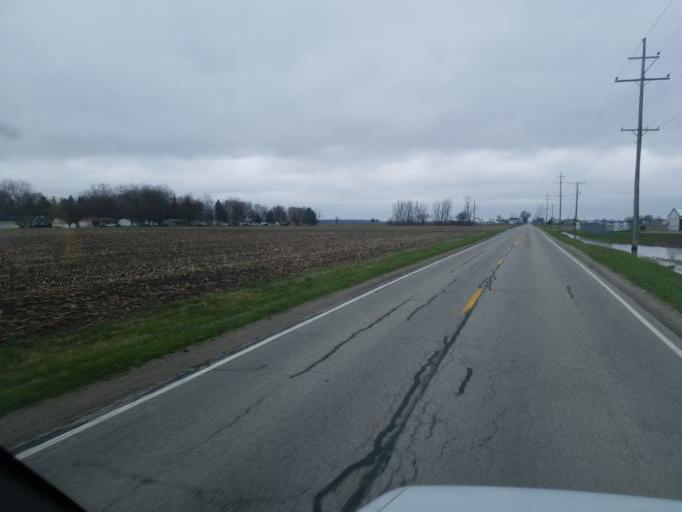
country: US
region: Ohio
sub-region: Marion County
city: Marion
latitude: 40.6470
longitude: -83.0732
